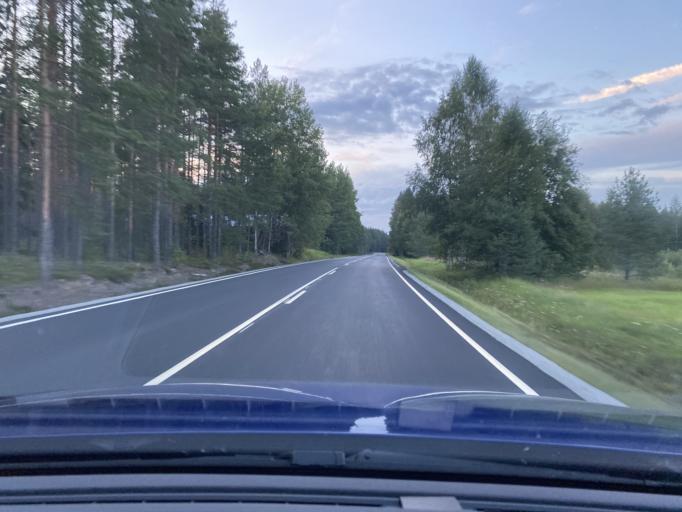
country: FI
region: Satakunta
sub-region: Pohjois-Satakunta
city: Honkajoki
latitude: 62.0651
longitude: 22.2486
